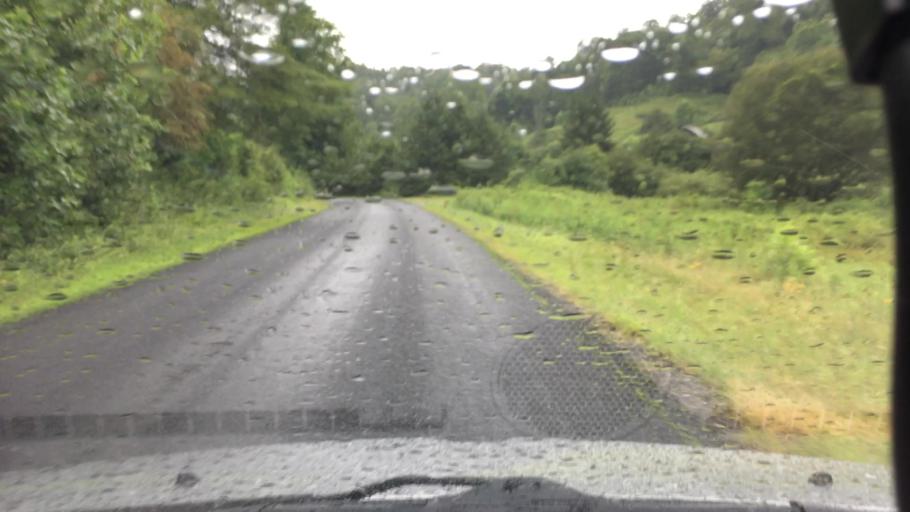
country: US
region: North Carolina
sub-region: Madison County
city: Mars Hill
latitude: 35.9109
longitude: -82.5183
